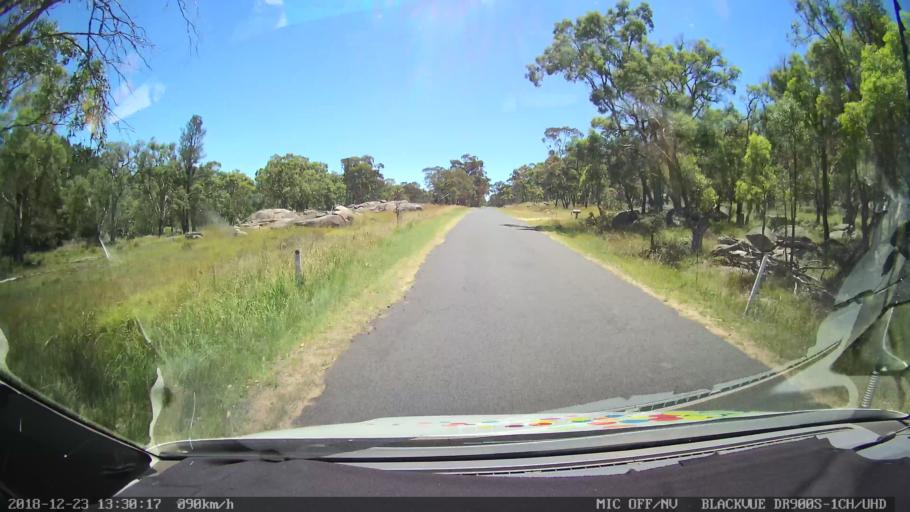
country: AU
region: New South Wales
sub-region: Armidale Dumaresq
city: Armidale
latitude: -30.4646
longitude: 151.3221
